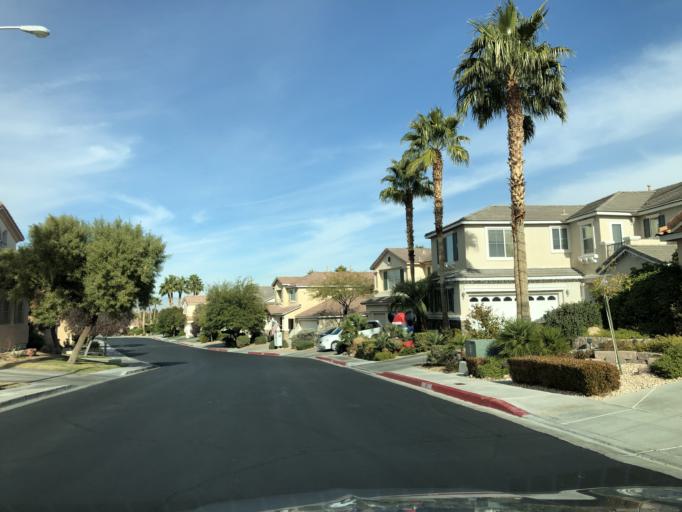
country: US
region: Nevada
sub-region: Clark County
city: Whitney
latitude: 36.0148
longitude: -115.0897
